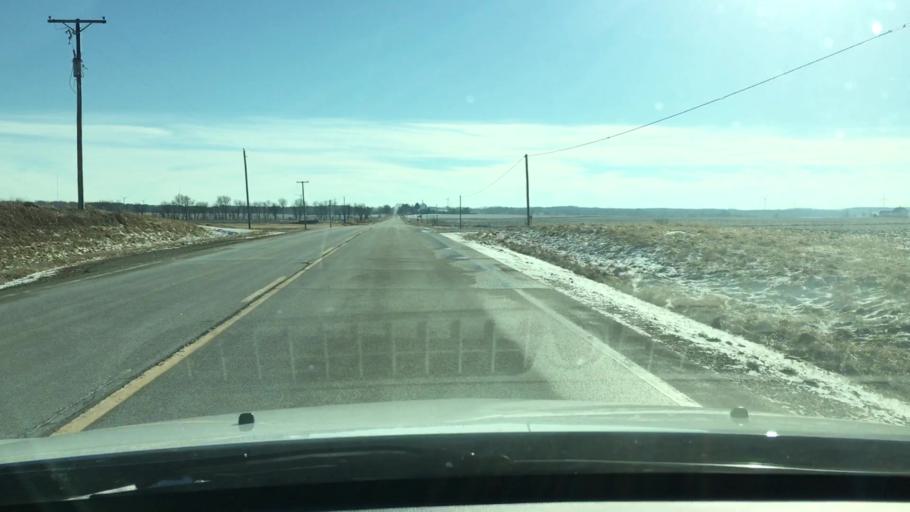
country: US
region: Illinois
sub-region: Ogle County
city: Rochelle
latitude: 41.7544
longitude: -89.0837
